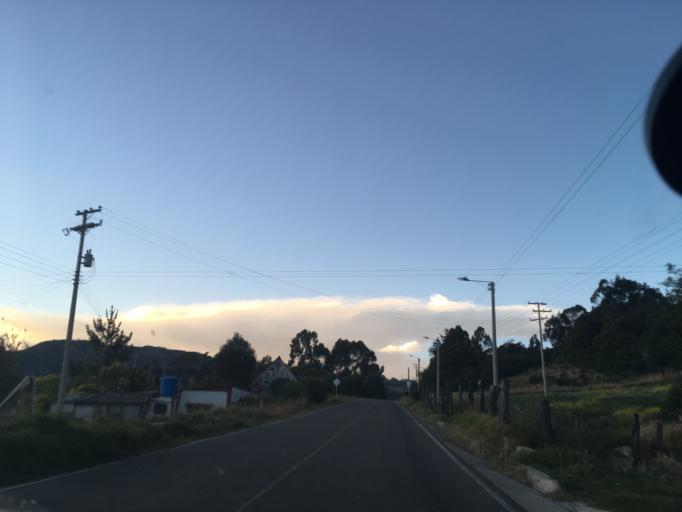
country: CO
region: Boyaca
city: Aquitania
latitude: 5.5896
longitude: -72.9028
